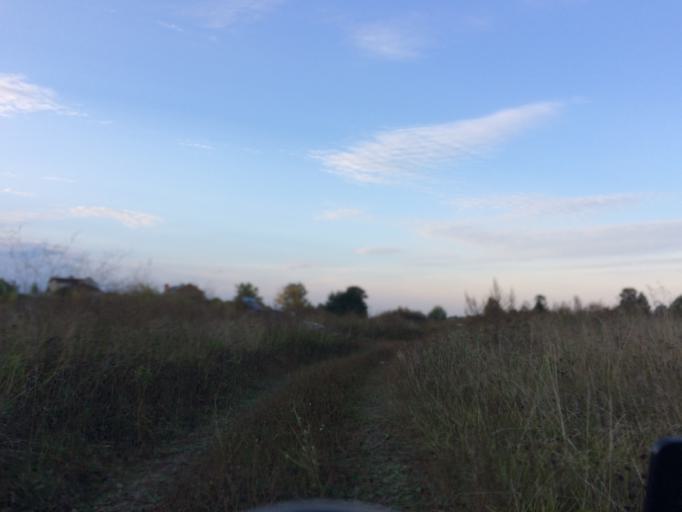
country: RU
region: Mariy-El
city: Yoshkar-Ola
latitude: 56.6487
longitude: 47.9206
